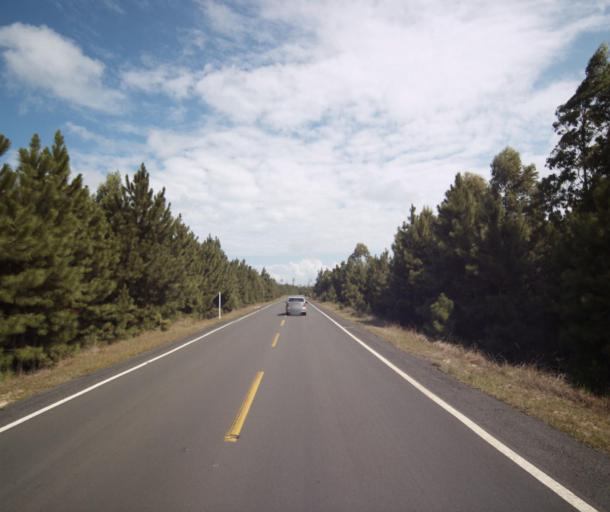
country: BR
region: Rio Grande do Sul
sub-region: Sao Lourenco Do Sul
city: Sao Lourenco do Sul
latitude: -31.4684
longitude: -51.2334
